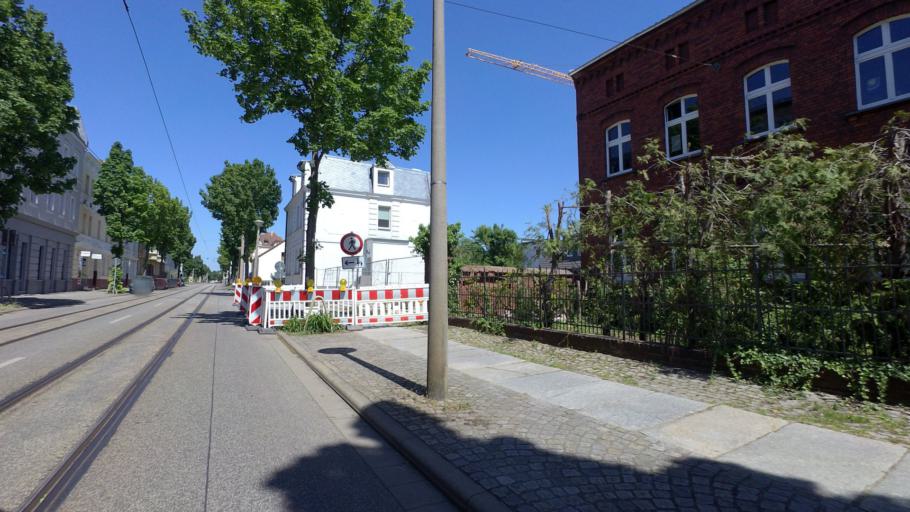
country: DE
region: Brandenburg
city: Cottbus
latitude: 51.7692
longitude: 14.3350
